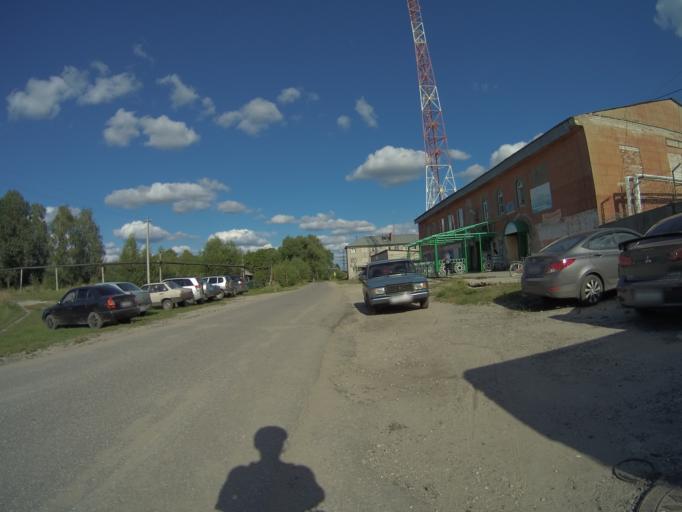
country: RU
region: Vladimir
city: Urshel'skiy
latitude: 55.6785
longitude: 40.2182
